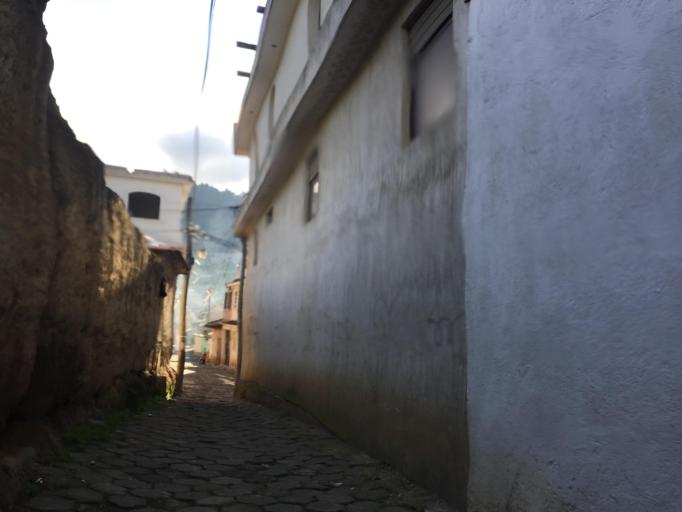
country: GT
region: Totonicapan
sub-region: Municipio de Totonicapan
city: Totonicapan
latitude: 14.9152
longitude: -91.3591
